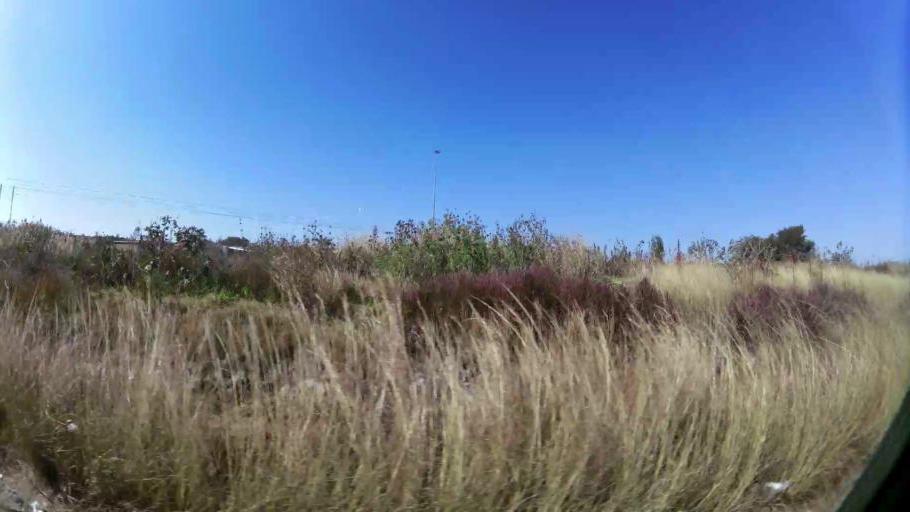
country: ZA
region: Gauteng
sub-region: City of Tshwane Metropolitan Municipality
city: Mabopane
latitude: -25.5492
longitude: 28.0744
